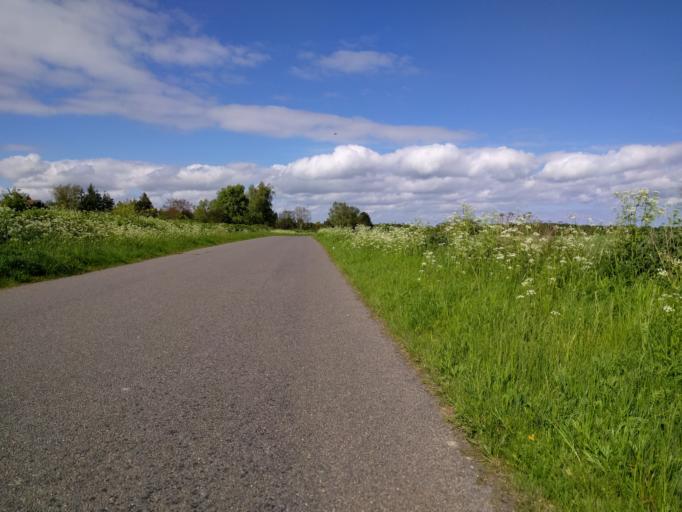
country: DK
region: Zealand
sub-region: Guldborgsund Kommune
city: Stubbekobing
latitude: 54.9184
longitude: 12.0642
